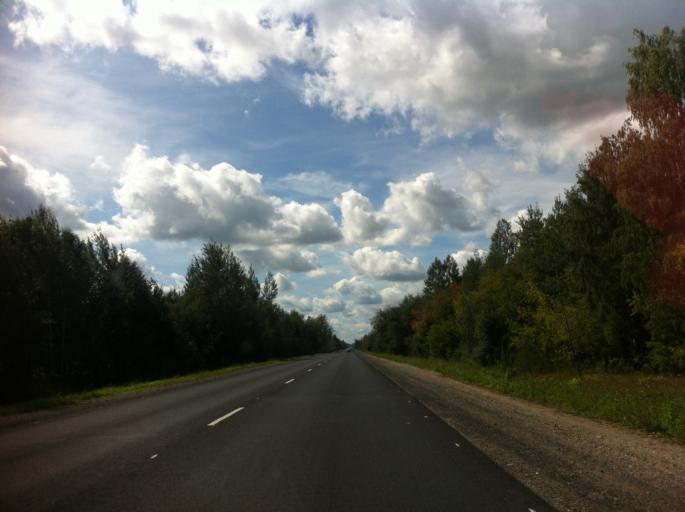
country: RU
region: Pskov
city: Izborsk
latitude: 57.7540
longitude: 28.0631
